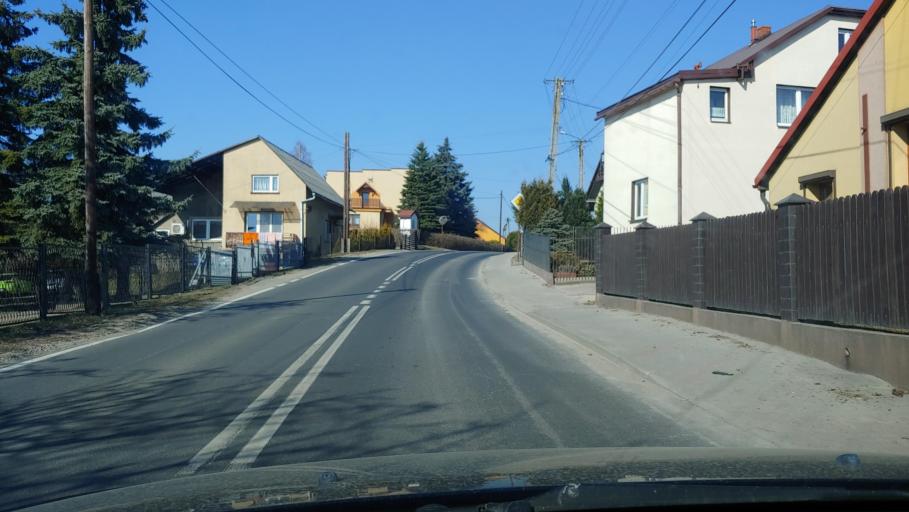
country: PL
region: Lesser Poland Voivodeship
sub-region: Powiat chrzanowski
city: Myslachowice
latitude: 50.1809
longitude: 19.4757
